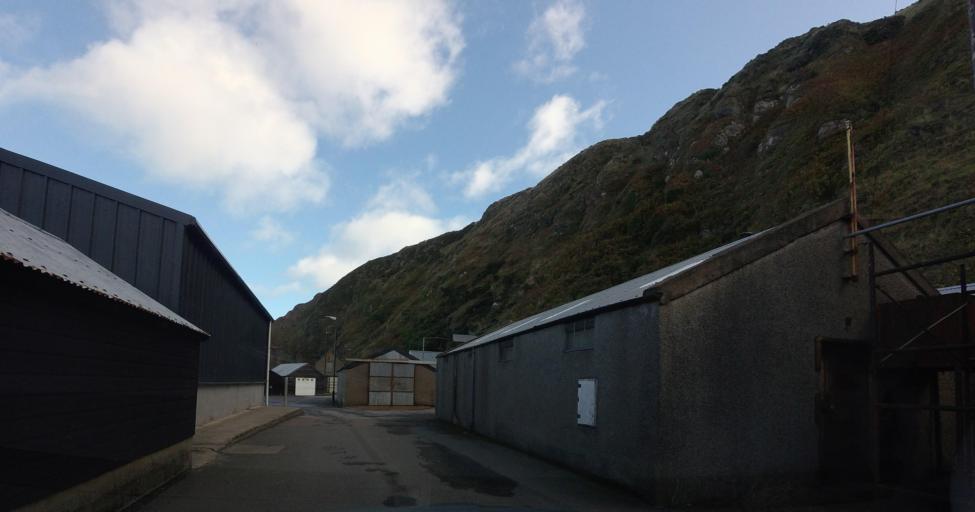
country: GB
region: Scotland
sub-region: Aberdeenshire
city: Macduff
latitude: 57.6735
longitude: -2.3350
